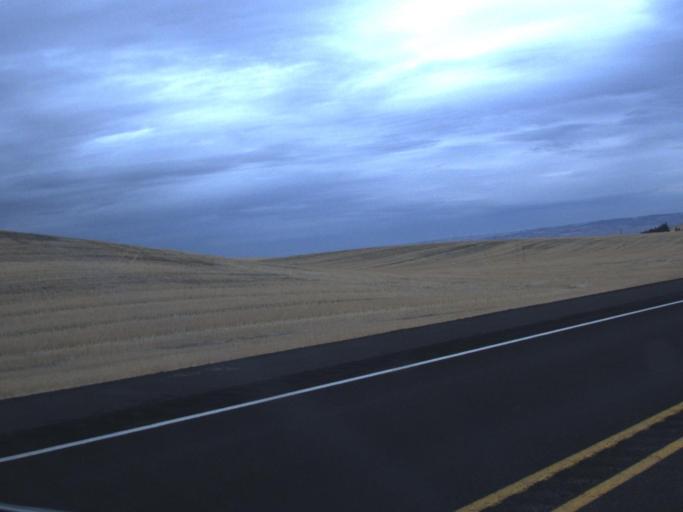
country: US
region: Washington
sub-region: Asotin County
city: Clarkston
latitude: 46.4804
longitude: -117.0556
